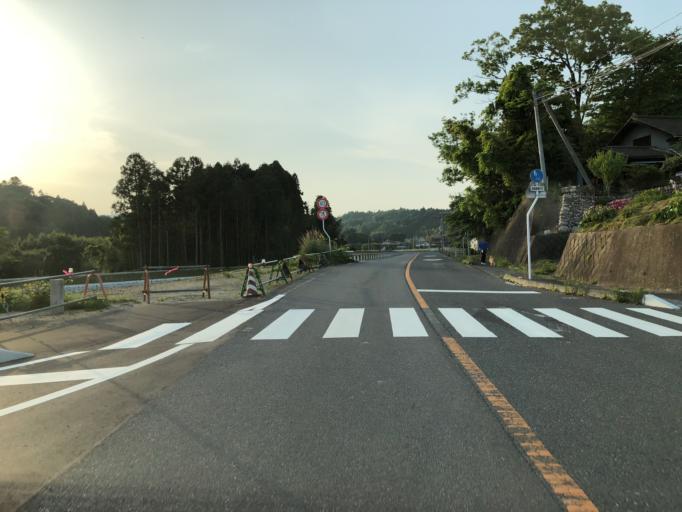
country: JP
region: Fukushima
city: Iwaki
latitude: 37.2100
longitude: 140.9865
